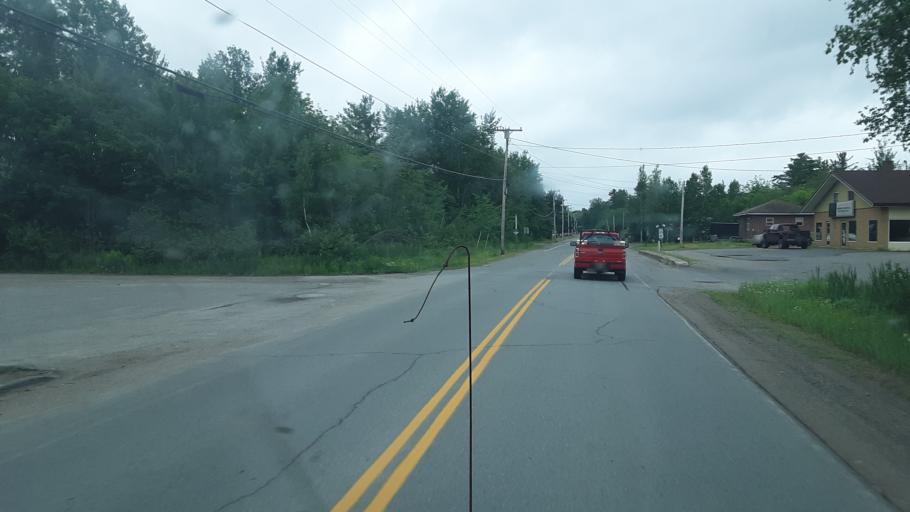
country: US
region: Maine
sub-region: Penobscot County
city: Millinocket
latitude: 45.6719
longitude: -68.7203
